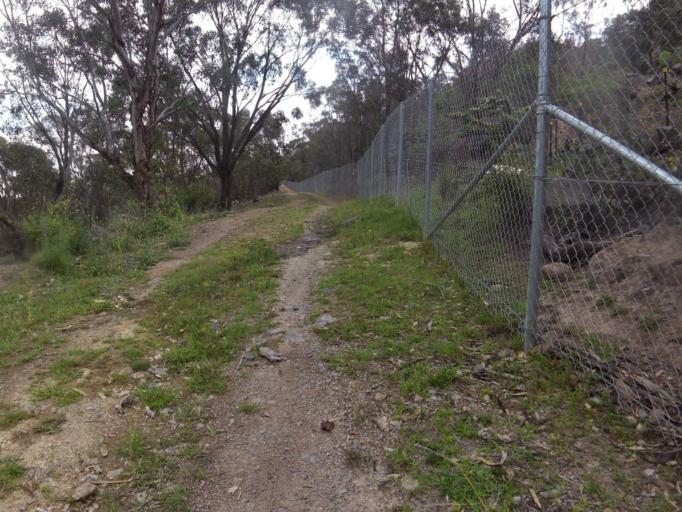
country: AU
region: Australian Capital Territory
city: Forrest
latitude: -35.3543
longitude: 149.1245
